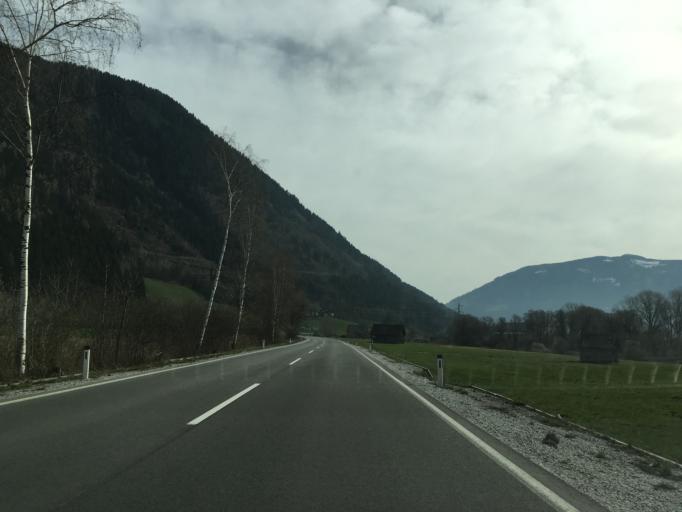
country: AT
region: Styria
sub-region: Politischer Bezirk Liezen
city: Liezen
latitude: 47.5616
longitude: 14.2661
